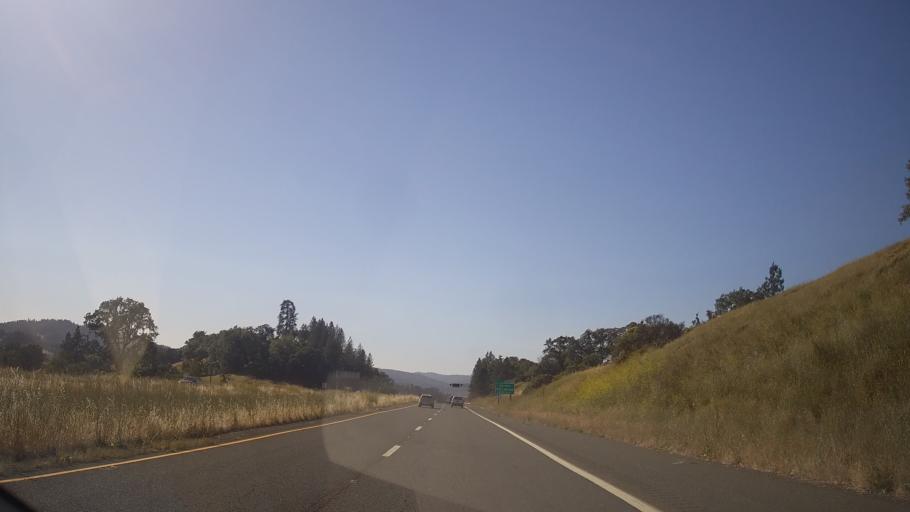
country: US
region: California
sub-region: Mendocino County
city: Willits
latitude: 39.3677
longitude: -123.3172
